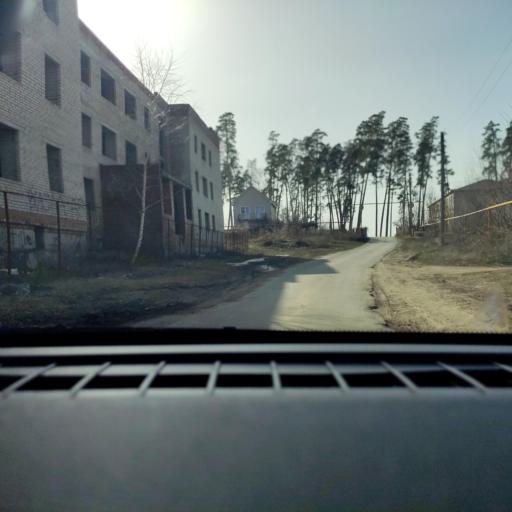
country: RU
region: Samara
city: Tol'yatti
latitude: 53.5017
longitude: 49.3559
